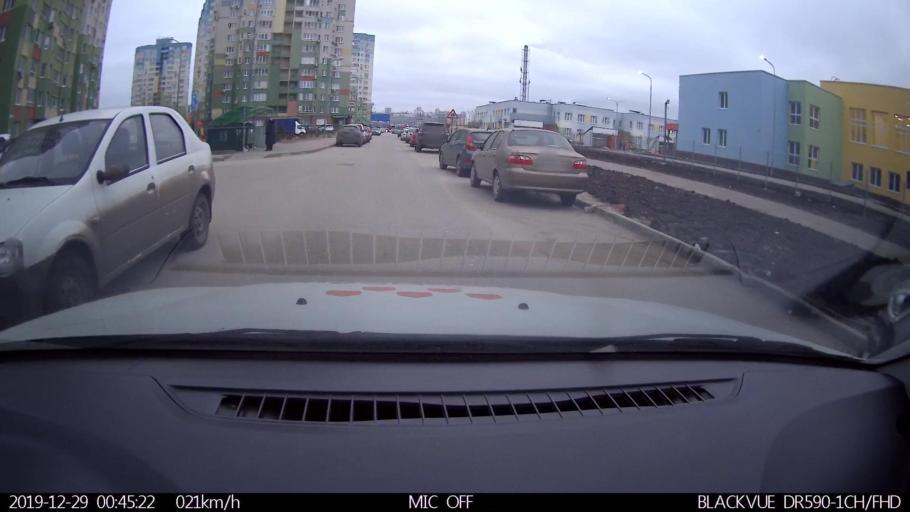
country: RU
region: Nizjnij Novgorod
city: Nizhniy Novgorod
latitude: 56.3404
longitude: 43.9484
